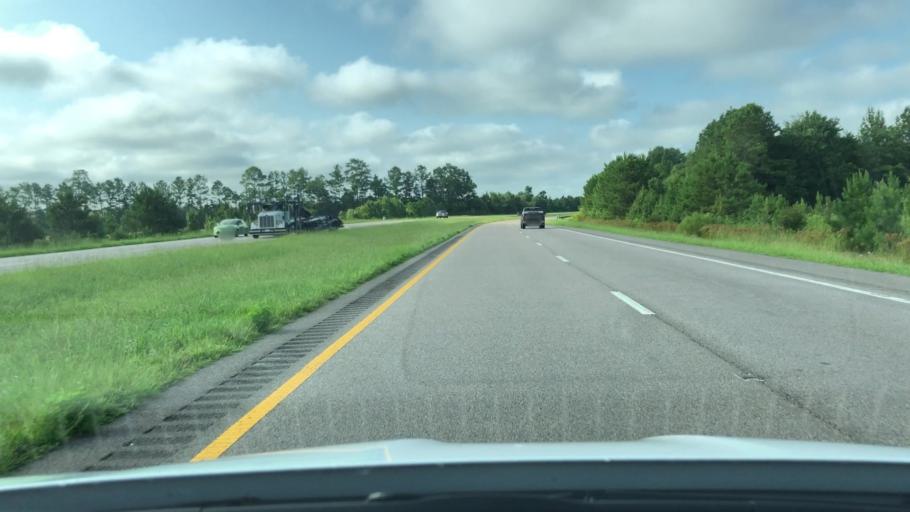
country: US
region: Virginia
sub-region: City of Portsmouth
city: Portsmouth Heights
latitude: 36.6808
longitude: -76.3473
